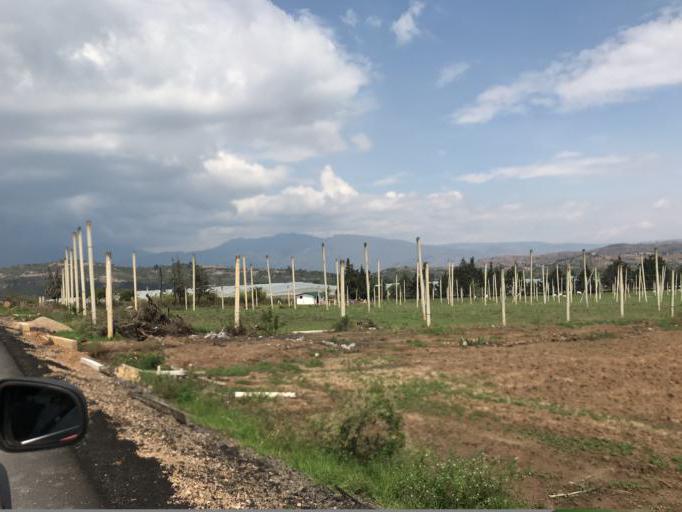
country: CO
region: Boyaca
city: Sutamarchan
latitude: 5.6327
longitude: -73.6040
